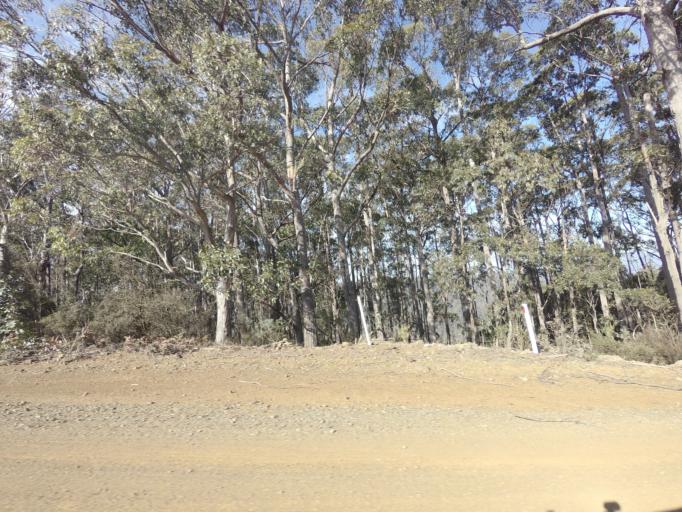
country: AU
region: Tasmania
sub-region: Sorell
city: Sorell
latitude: -42.4978
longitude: 147.4803
